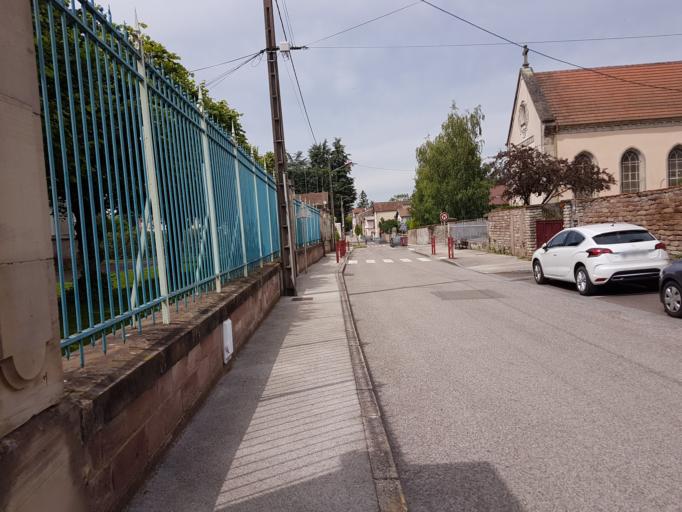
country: FR
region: Franche-Comte
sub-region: Departement de la Haute-Saone
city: Luxeuil-les-Bains
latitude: 47.8170
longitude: 6.3779
